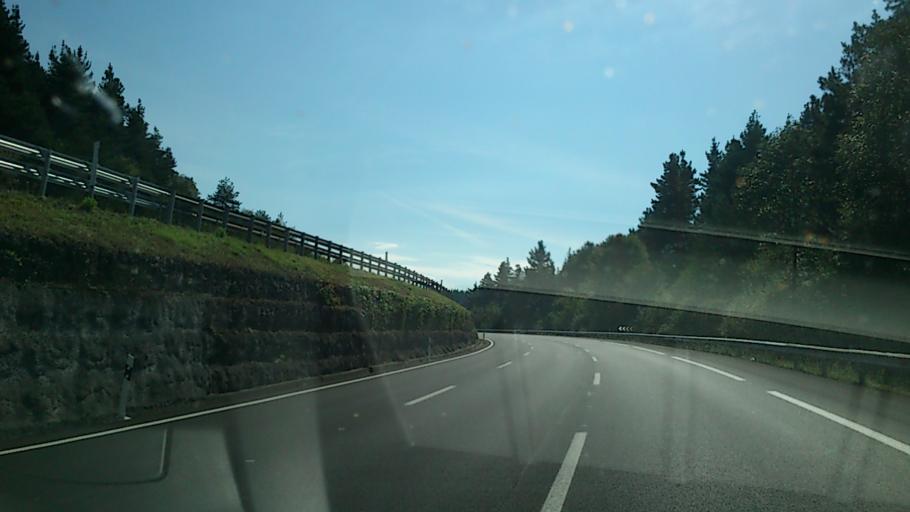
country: ES
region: Basque Country
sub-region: Provincia de Alava
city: Lezama
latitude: 43.0228
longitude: -2.9126
